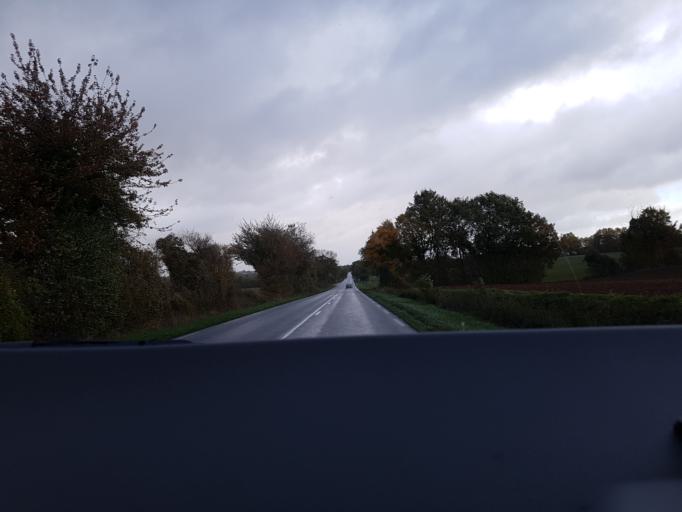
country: FR
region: Poitou-Charentes
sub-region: Departement des Deux-Sevres
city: Melle
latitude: 46.1967
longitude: -0.1676
